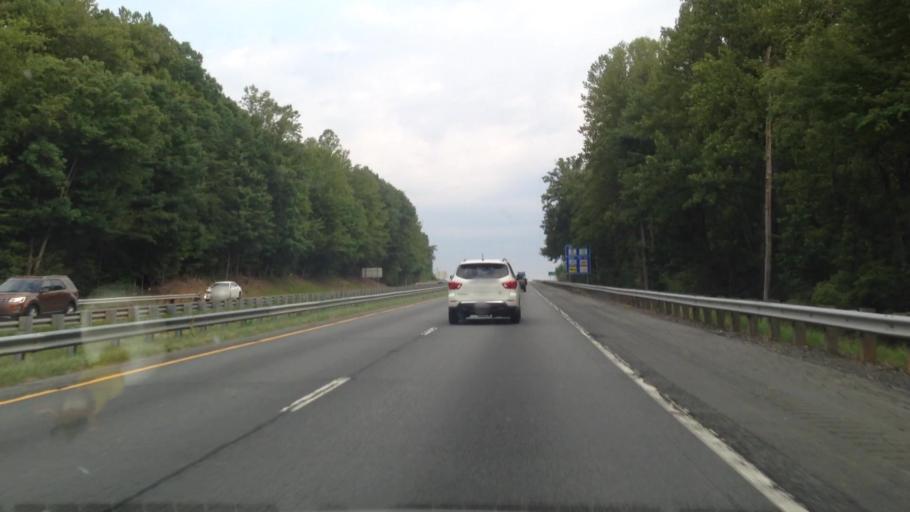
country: US
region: North Carolina
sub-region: Forsyth County
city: Tobaccoville
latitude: 36.2534
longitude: -80.3579
